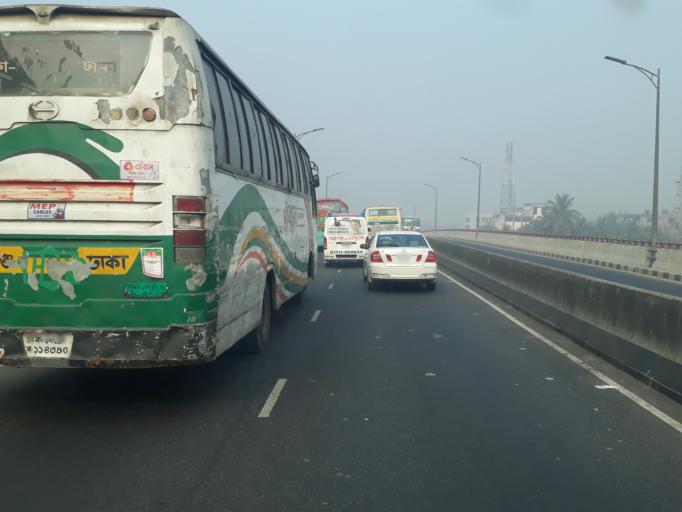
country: BD
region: Dhaka
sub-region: Dhaka
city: Dhaka
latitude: 23.7085
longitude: 90.4378
